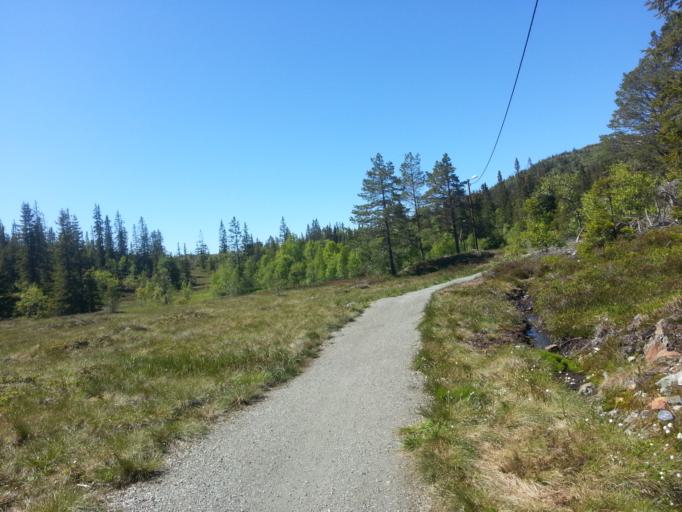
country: NO
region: Sor-Trondelag
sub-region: Melhus
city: Melhus
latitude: 63.4136
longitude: 10.2668
